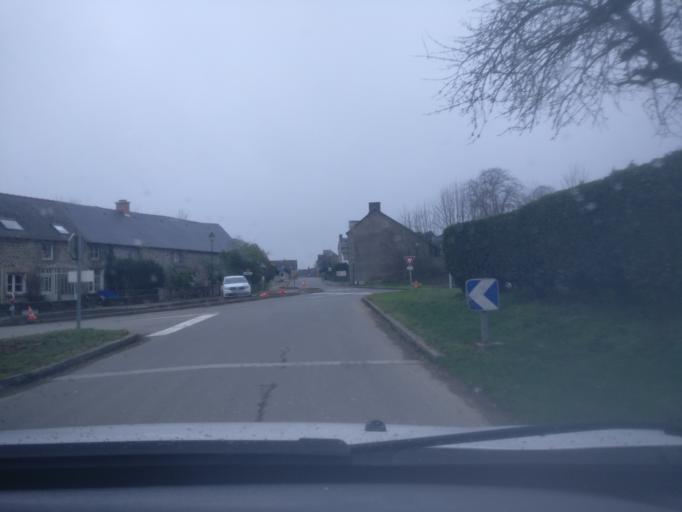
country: FR
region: Brittany
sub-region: Departement d'Ille-et-Vilaine
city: Saint-Medard-sur-Ille
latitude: 48.2967
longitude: -1.6355
